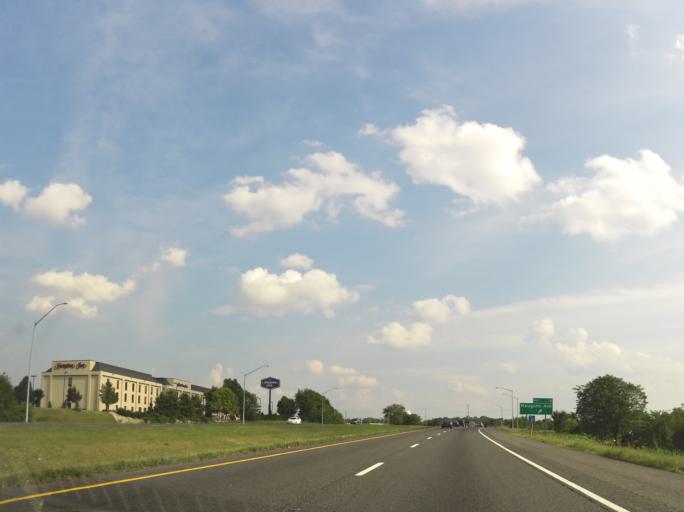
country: US
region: Maryland
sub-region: Washington County
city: Maugansville
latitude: 39.6930
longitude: -77.7346
